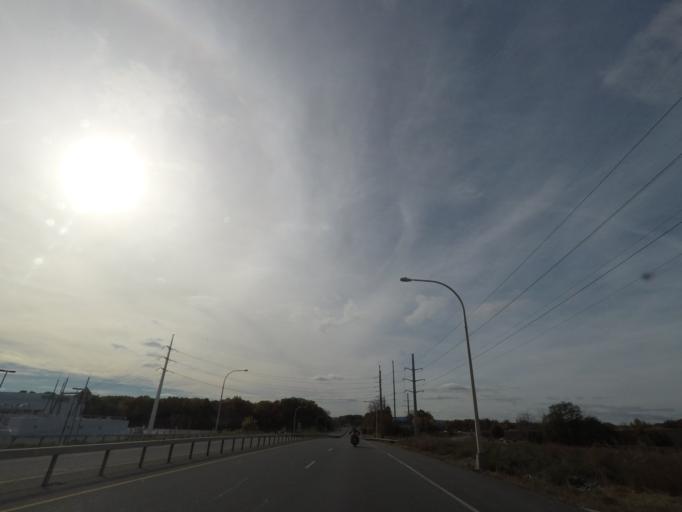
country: US
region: New York
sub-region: Albany County
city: McKownville
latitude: 42.6935
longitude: -73.8355
